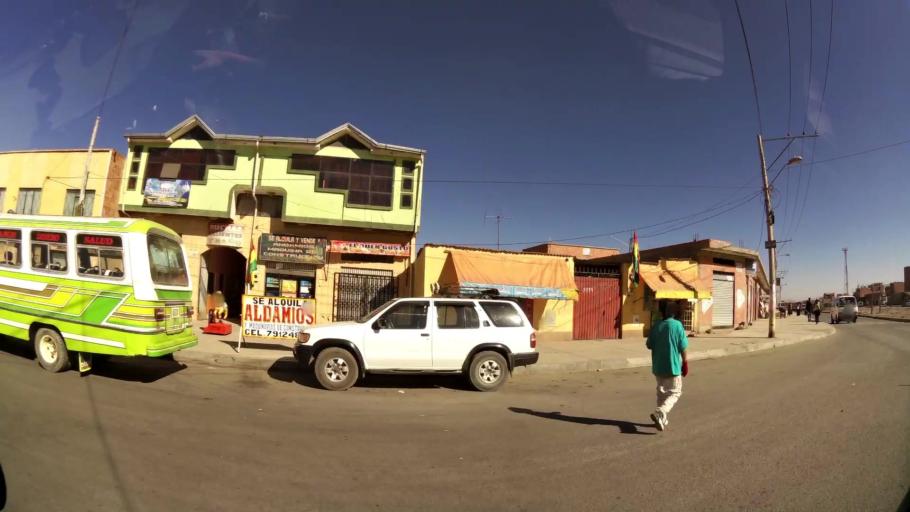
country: BO
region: La Paz
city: La Paz
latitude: -16.5257
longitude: -68.2178
